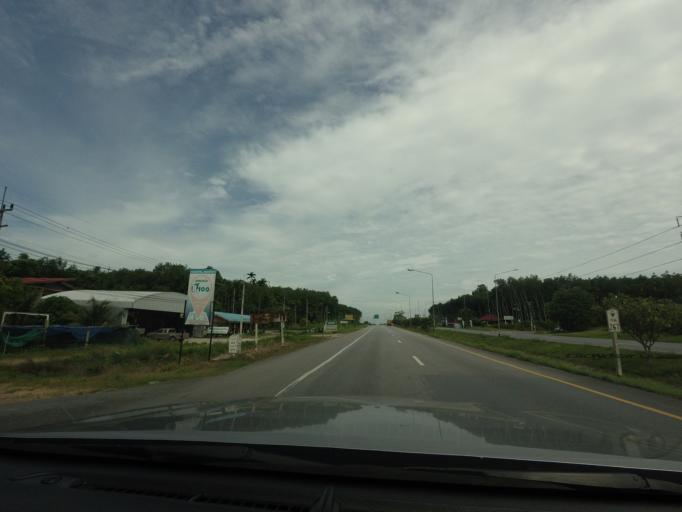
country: TH
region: Nakhon Si Thammarat
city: Thung Yai
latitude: 8.3167
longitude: 99.4684
